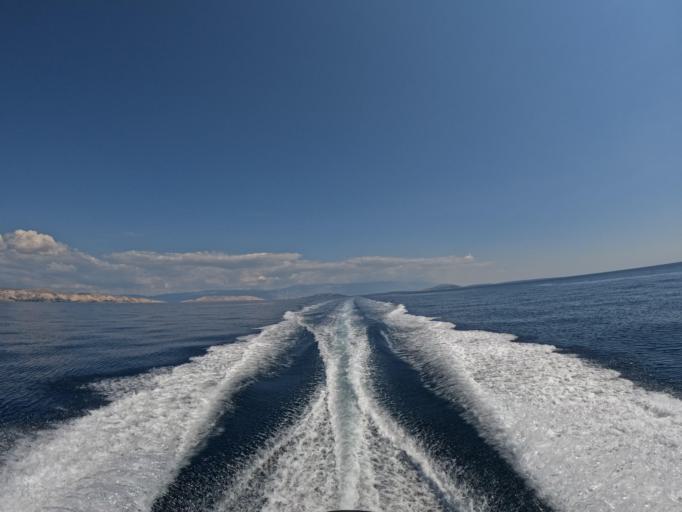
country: HR
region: Primorsko-Goranska
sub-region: Grad Krk
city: Krk
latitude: 44.9185
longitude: 14.5710
